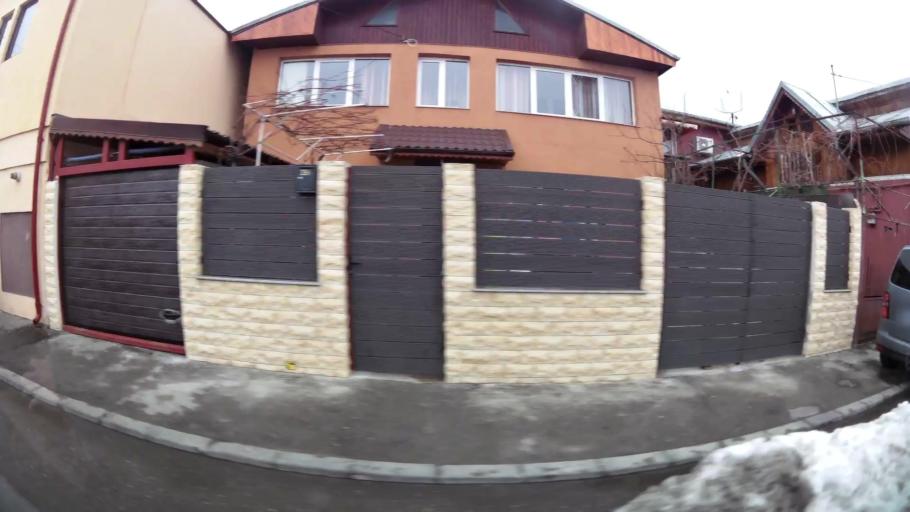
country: RO
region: Ilfov
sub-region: Comuna Pantelimon
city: Pantelimon
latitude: 44.4308
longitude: 26.2045
